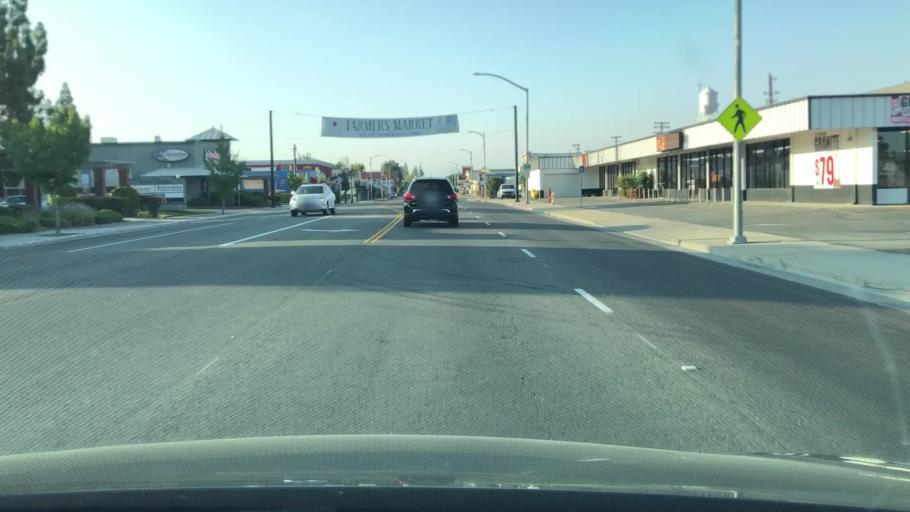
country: US
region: California
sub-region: Fresno County
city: Clovis
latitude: 36.8207
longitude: -119.7006
